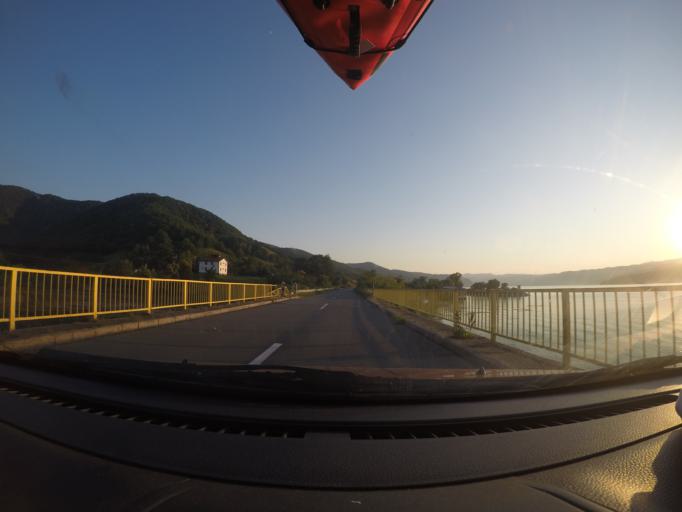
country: RO
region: Mehedinti
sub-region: Comuna Eselnita
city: Eselnita
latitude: 44.6788
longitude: 22.4017
